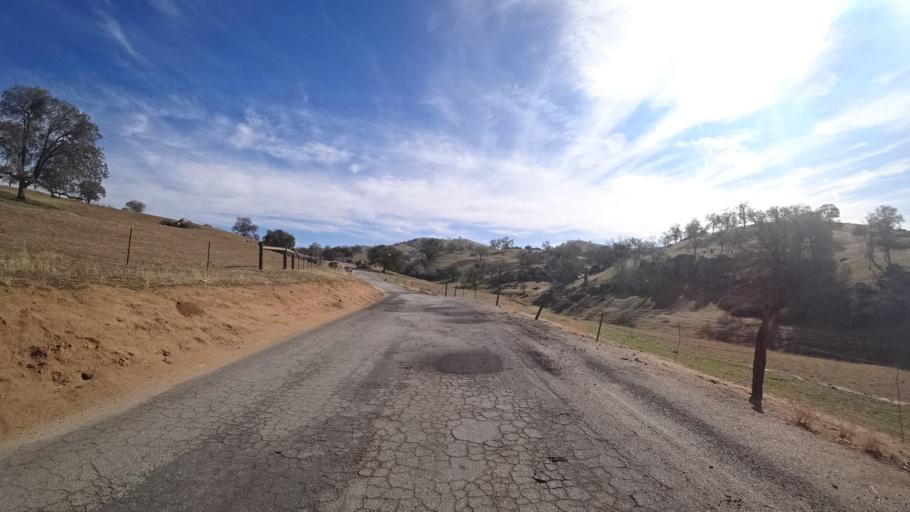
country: US
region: California
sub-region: Kern County
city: Oildale
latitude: 35.6147
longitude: -118.8455
